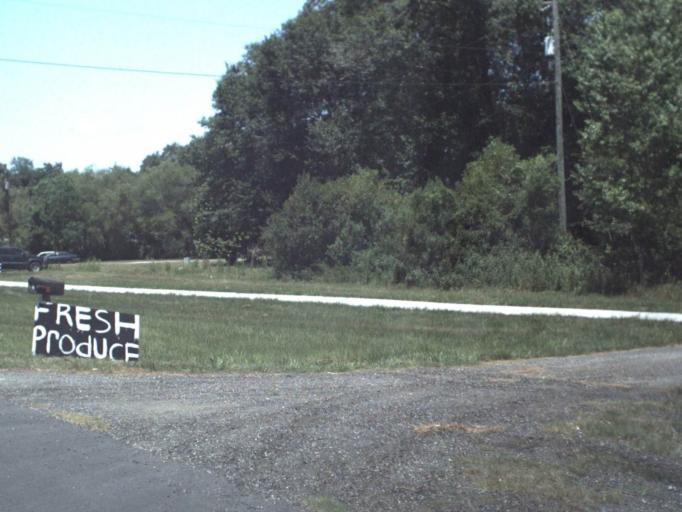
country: US
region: Florida
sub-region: Union County
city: Lake Butler
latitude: 30.0672
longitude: -82.2294
